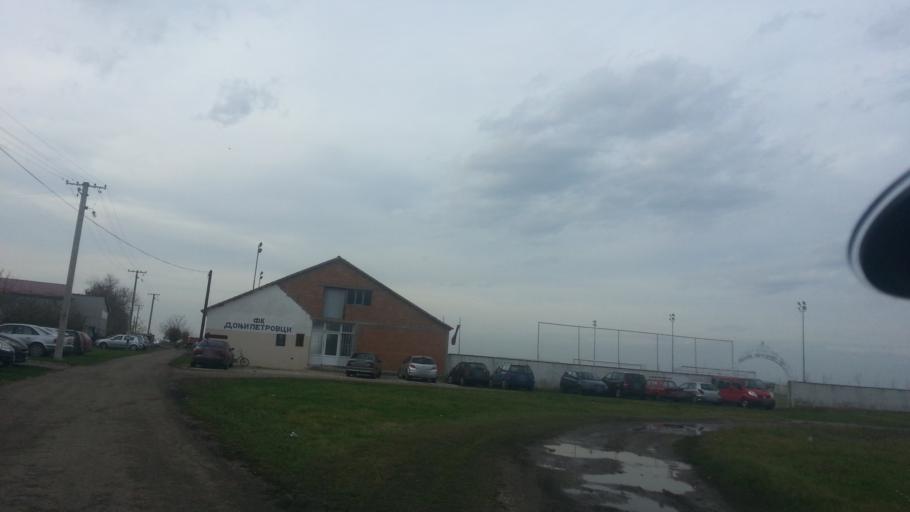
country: RS
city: Putinci
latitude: 44.9670
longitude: 19.9814
